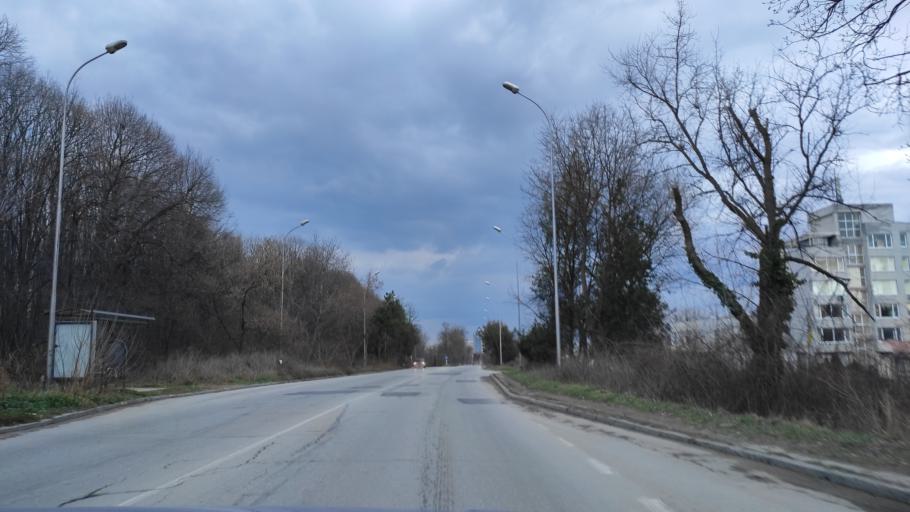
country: BG
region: Varna
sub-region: Obshtina Aksakovo
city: Aksakovo
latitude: 43.2246
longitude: 27.8630
